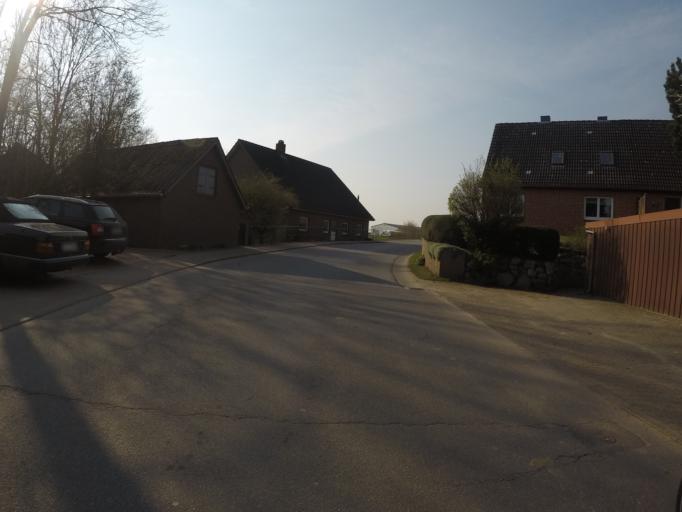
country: DE
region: Schleswig-Holstein
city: Leezen
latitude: 53.8709
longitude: 10.2458
